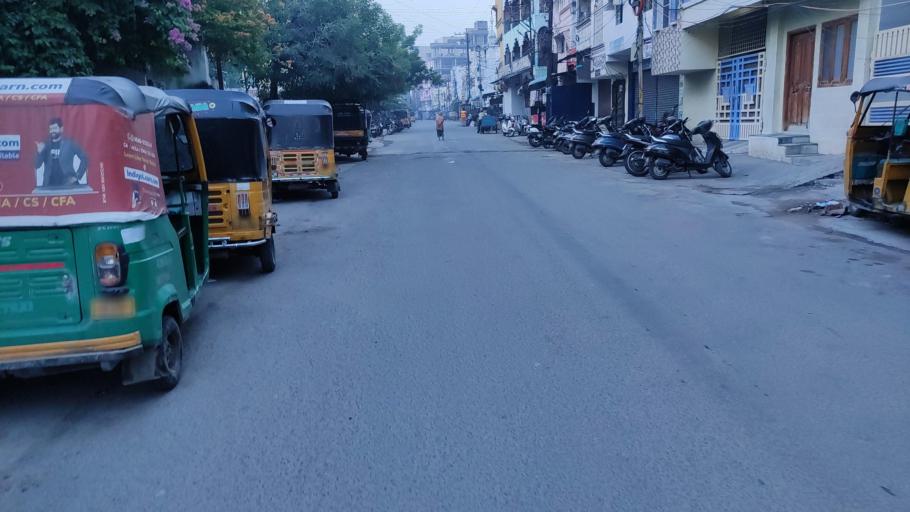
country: IN
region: Telangana
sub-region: Rangareddi
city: Gaddi Annaram
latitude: 17.3709
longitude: 78.4921
